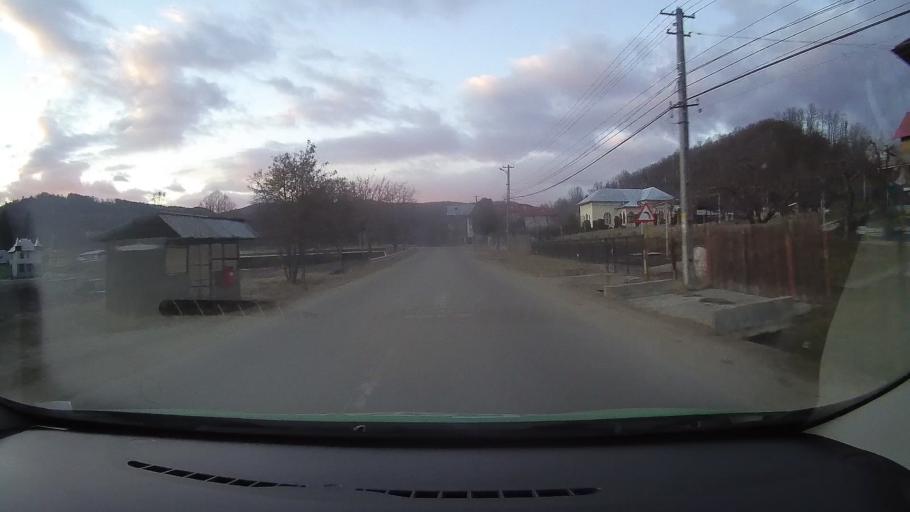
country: RO
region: Dambovita
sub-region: Comuna Valea Lunga
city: Valea Lunga-Cricov
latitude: 45.0692
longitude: 25.5810
